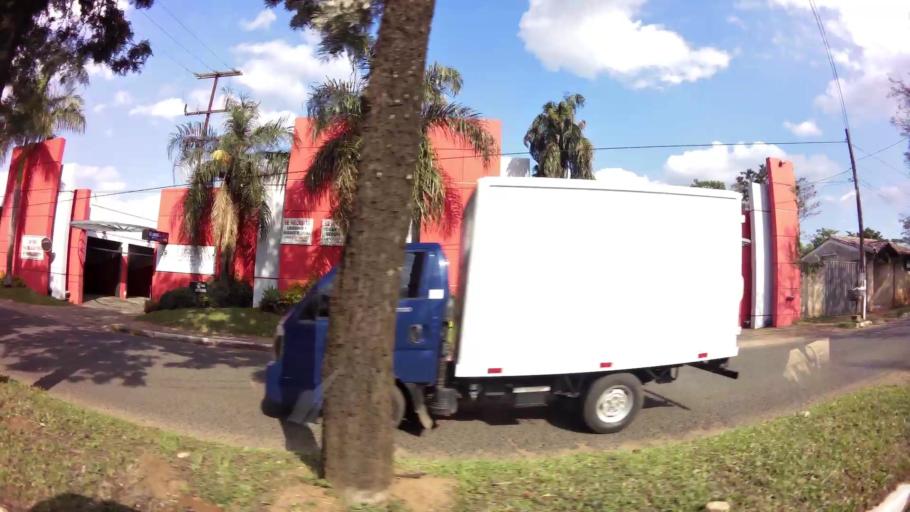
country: PY
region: Central
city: Fernando de la Mora
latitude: -25.3420
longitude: -57.5403
